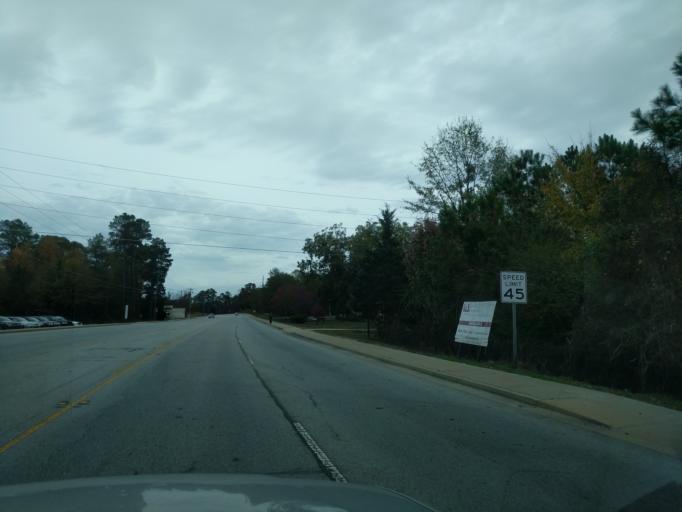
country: US
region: South Carolina
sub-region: Newberry County
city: Newberry
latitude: 34.3101
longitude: -81.6179
